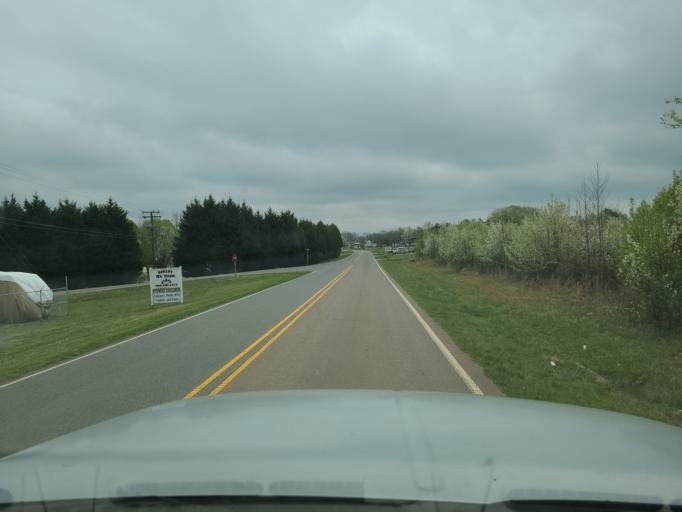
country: US
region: North Carolina
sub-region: Cleveland County
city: Shelby
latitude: 35.3727
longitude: -81.5990
